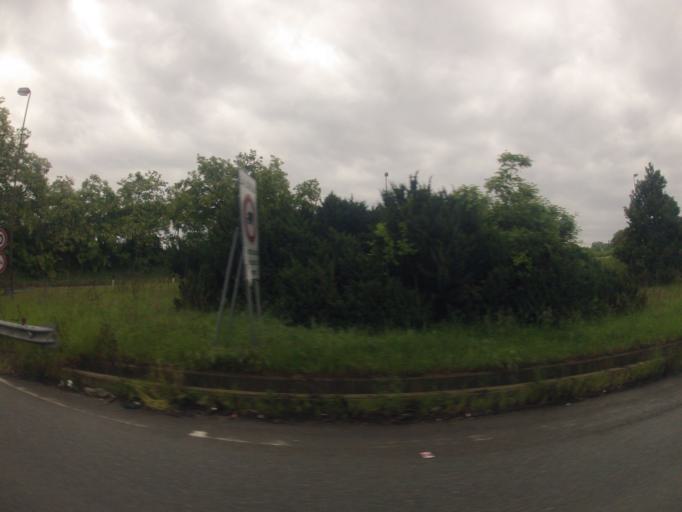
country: IT
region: Piedmont
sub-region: Provincia di Torino
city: La Loggia
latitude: 44.9523
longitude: 7.6792
